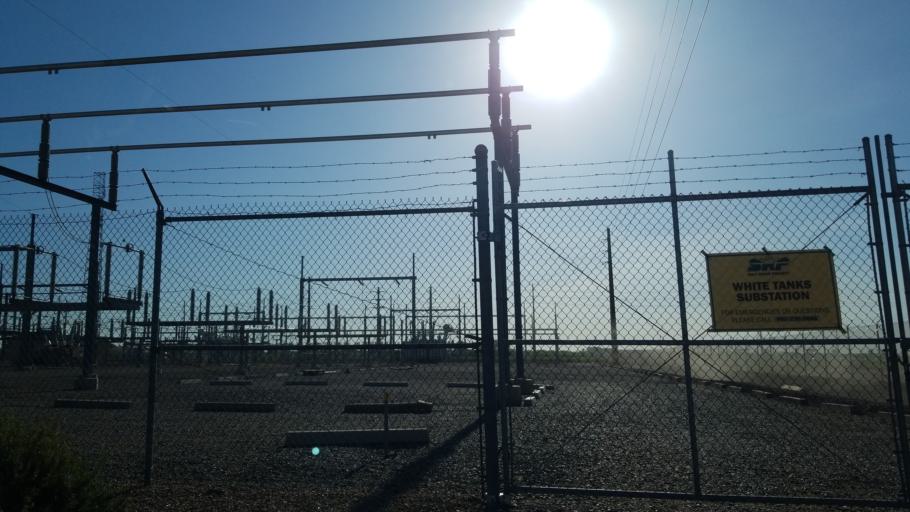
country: US
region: Arizona
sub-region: Maricopa County
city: Avondale
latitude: 33.4657
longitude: -112.3141
